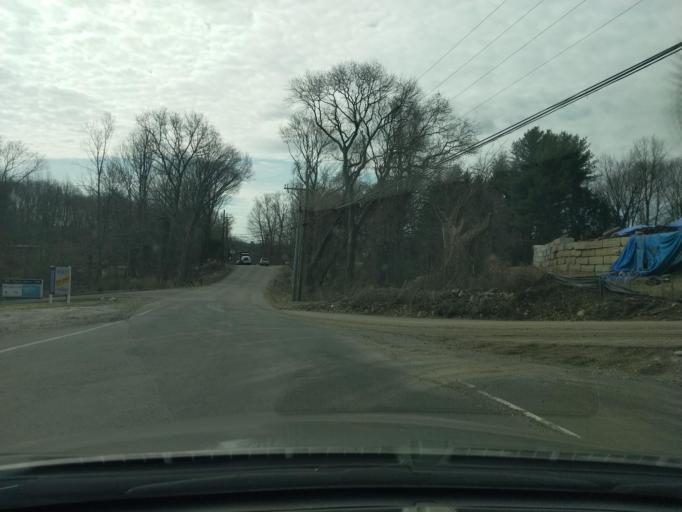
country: US
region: Connecticut
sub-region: Fairfield County
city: Newtown
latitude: 41.3457
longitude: -73.2504
